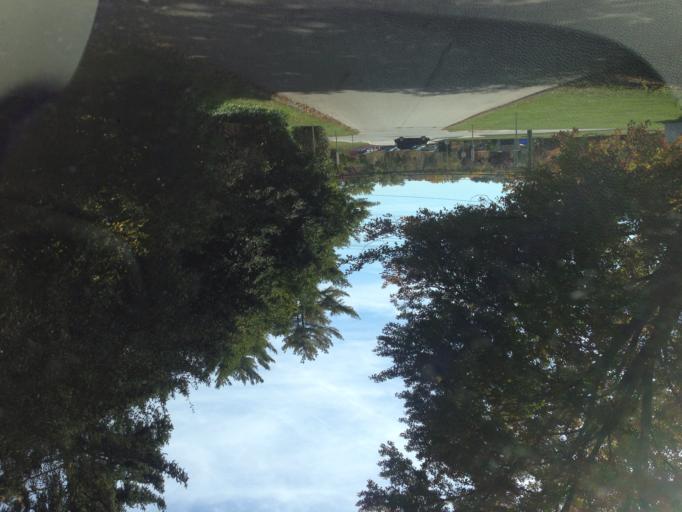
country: US
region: Maryland
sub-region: Howard County
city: Columbia
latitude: 39.2742
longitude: -76.8398
